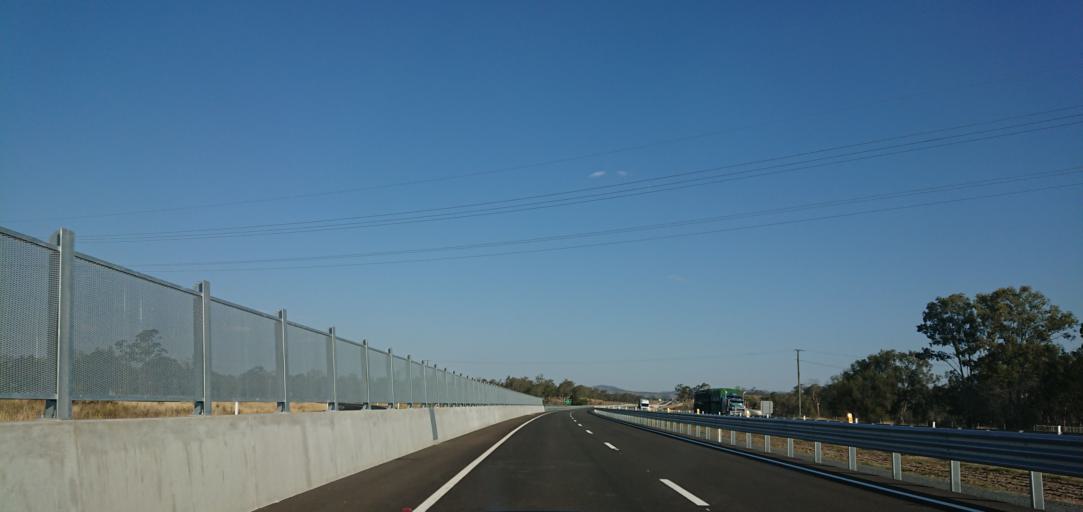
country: AU
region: Queensland
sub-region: Toowoomba
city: East Toowoomba
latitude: -27.5308
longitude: 152.0725
